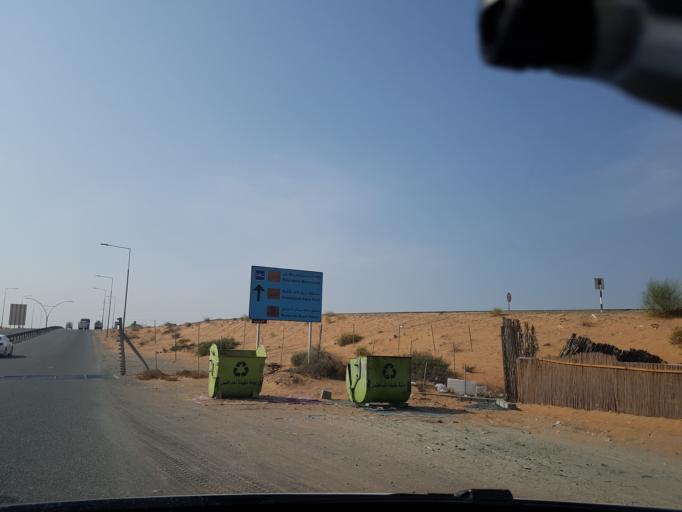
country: AE
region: Umm al Qaywayn
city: Umm al Qaywayn
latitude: 25.5287
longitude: 55.7224
